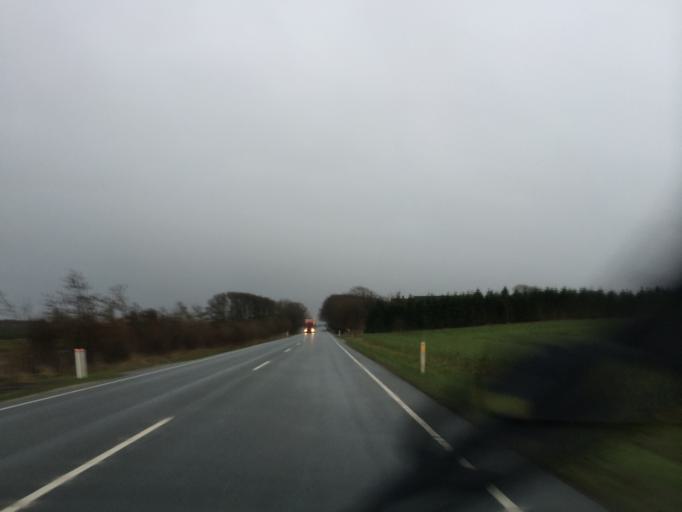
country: DK
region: South Denmark
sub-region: Varde Kommune
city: Varde
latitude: 55.6907
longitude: 8.4929
